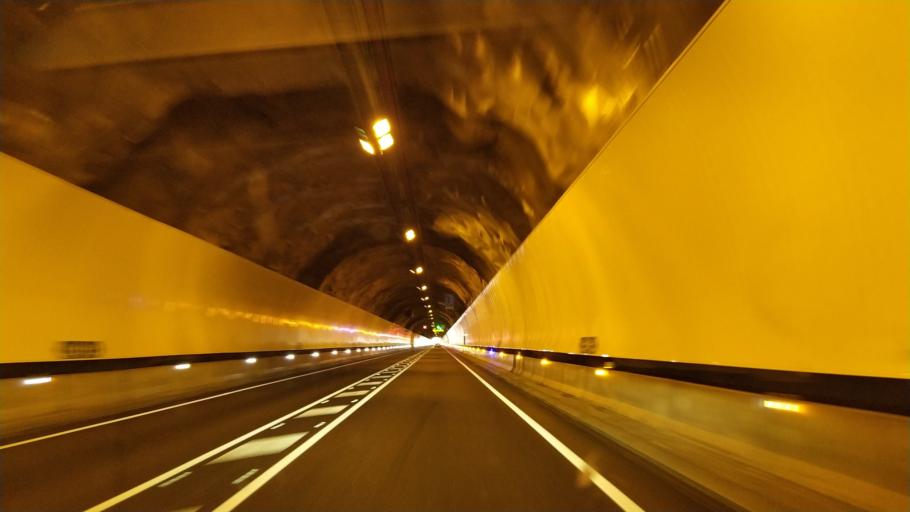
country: ES
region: Catalonia
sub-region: Provincia de Lleida
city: Coll de Nargo
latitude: 42.1363
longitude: 1.3093
